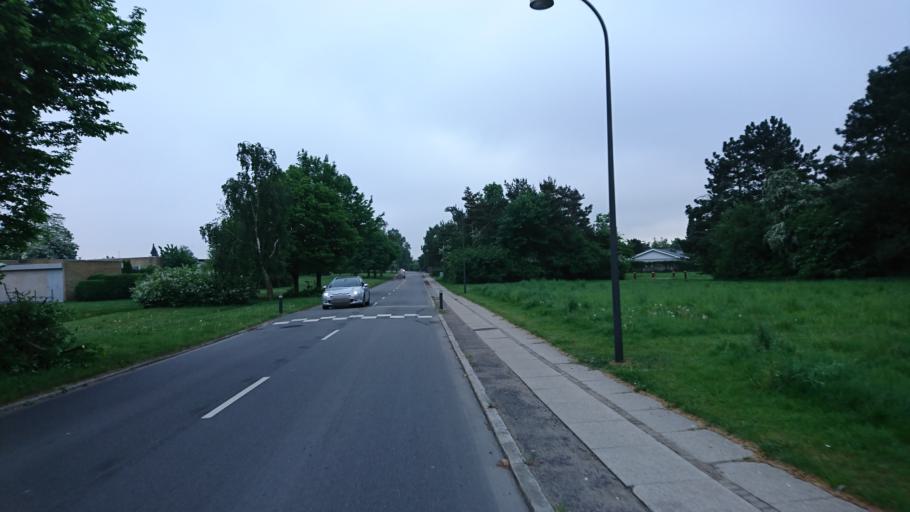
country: DK
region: Capital Region
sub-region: Herlev Kommune
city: Herlev
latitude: 55.7318
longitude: 12.4104
